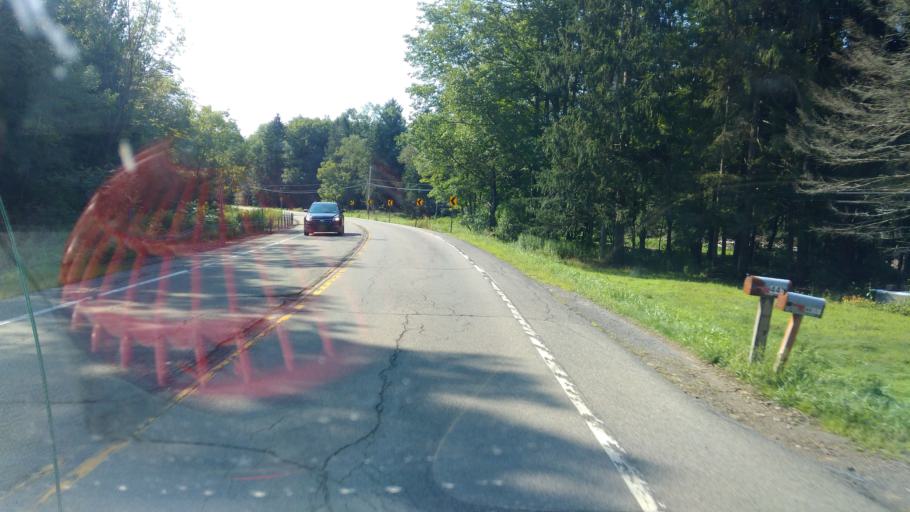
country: US
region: New York
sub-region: Allegany County
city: Cuba
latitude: 42.1929
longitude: -78.2671
